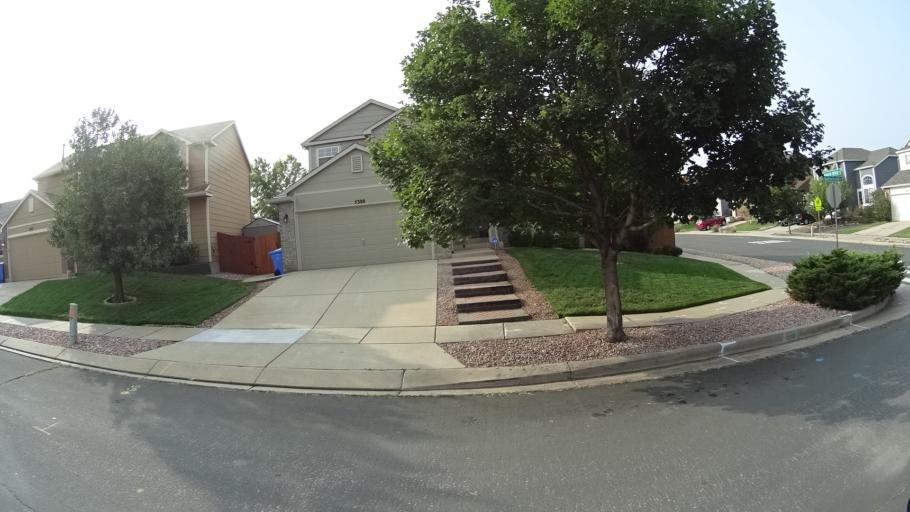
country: US
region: Colorado
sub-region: El Paso County
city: Black Forest
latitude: 38.9363
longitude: -104.7301
